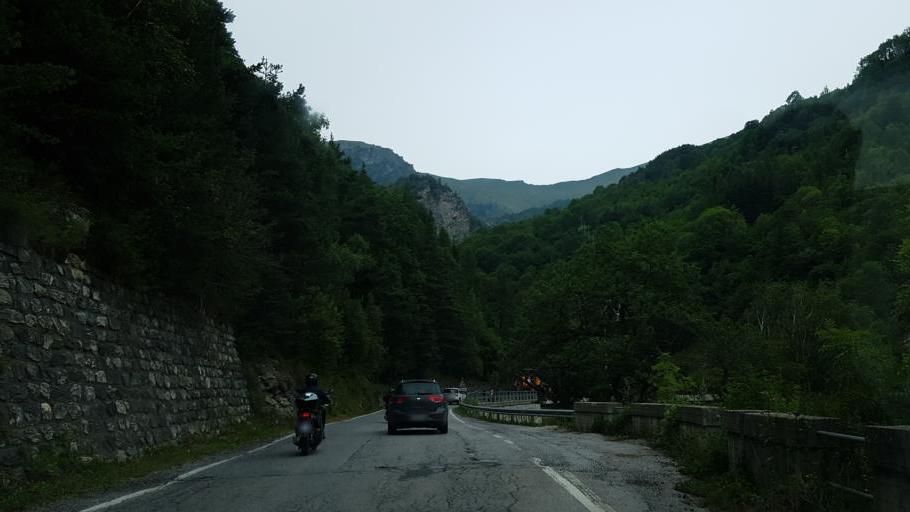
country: IT
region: Piedmont
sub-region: Provincia di Cuneo
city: Stroppo
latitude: 44.5028
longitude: 7.1223
